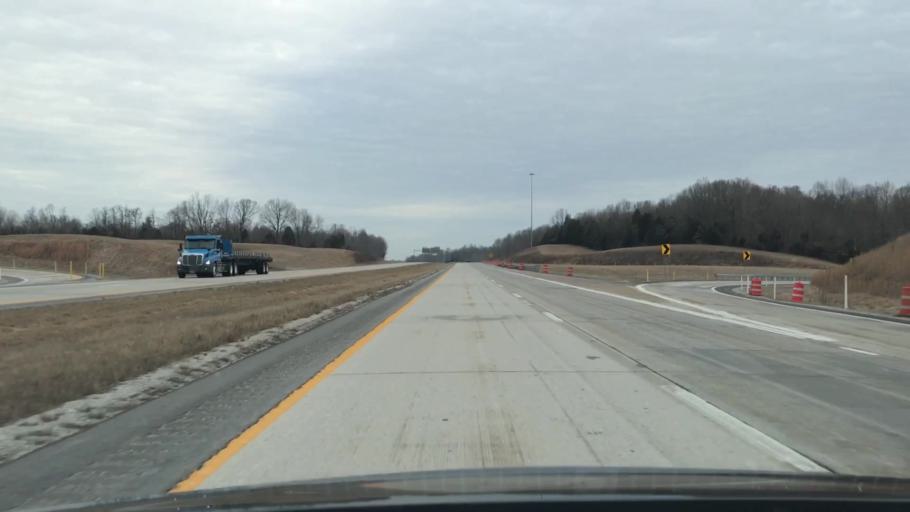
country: US
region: Kentucky
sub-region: Ohio County
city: Oak Grove
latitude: 37.3852
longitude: -86.8094
